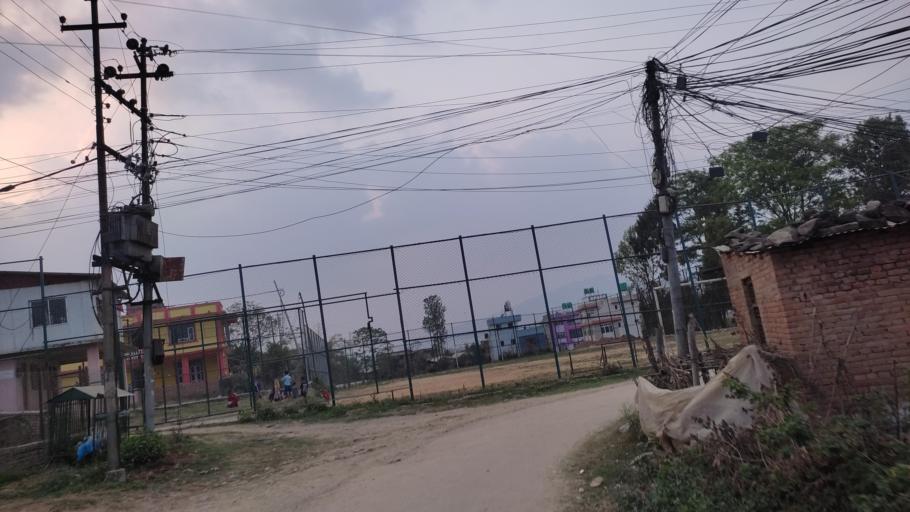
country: NP
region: Central Region
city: Kirtipur
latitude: 27.6682
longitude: 85.2628
